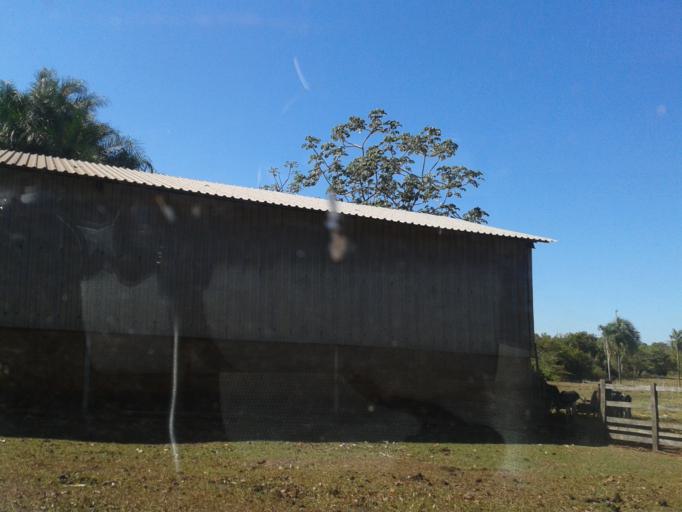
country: BR
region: Minas Gerais
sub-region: Centralina
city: Centralina
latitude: -18.5671
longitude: -49.1324
